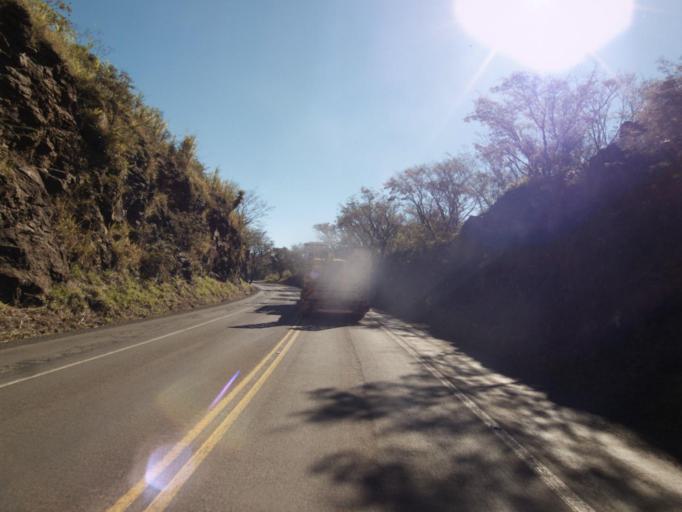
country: BR
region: Rio Grande do Sul
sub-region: Frederico Westphalen
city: Frederico Westphalen
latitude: -26.8052
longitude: -53.4416
